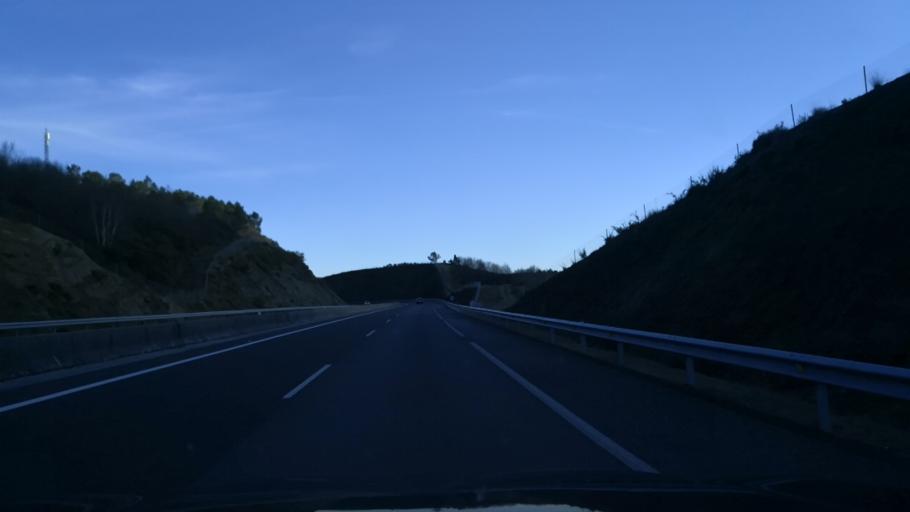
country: ES
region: Galicia
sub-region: Provincia de Pontevedra
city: Dozon
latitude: 42.5937
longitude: -8.0853
